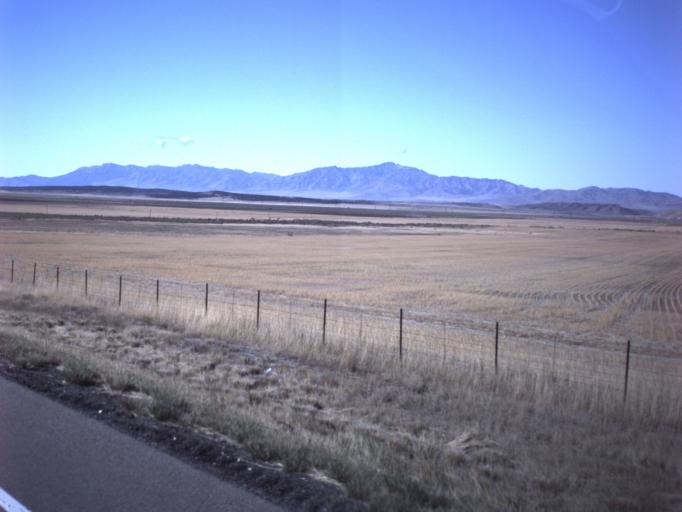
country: US
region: Utah
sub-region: Juab County
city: Nephi
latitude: 39.4936
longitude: -111.8807
